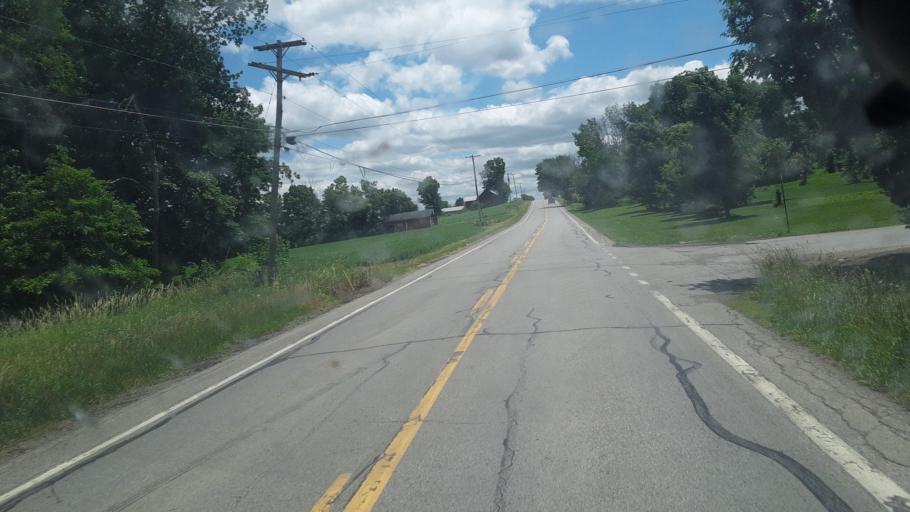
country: US
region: Pennsylvania
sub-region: Butler County
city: Slippery Rock
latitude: 41.0585
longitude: -80.2018
